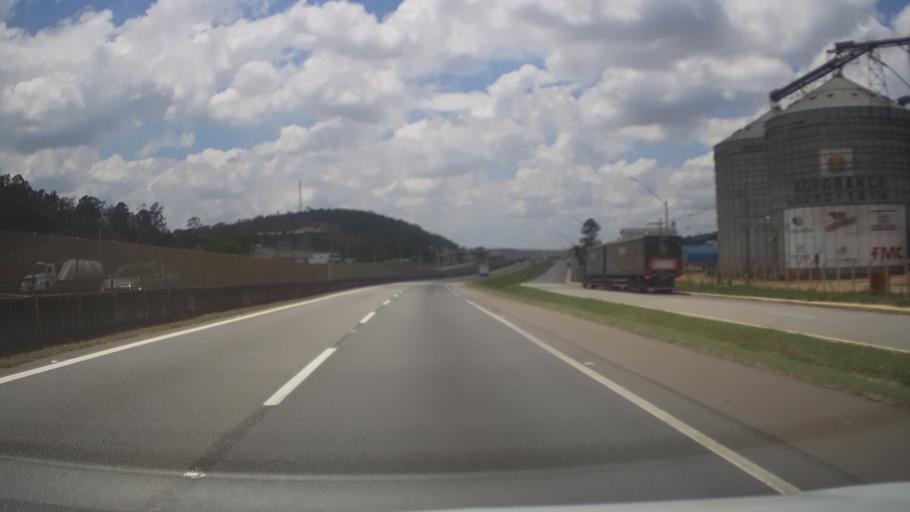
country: BR
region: Minas Gerais
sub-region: Tres Coracoes
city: Tres Coracoes
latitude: -21.6684
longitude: -45.3239
